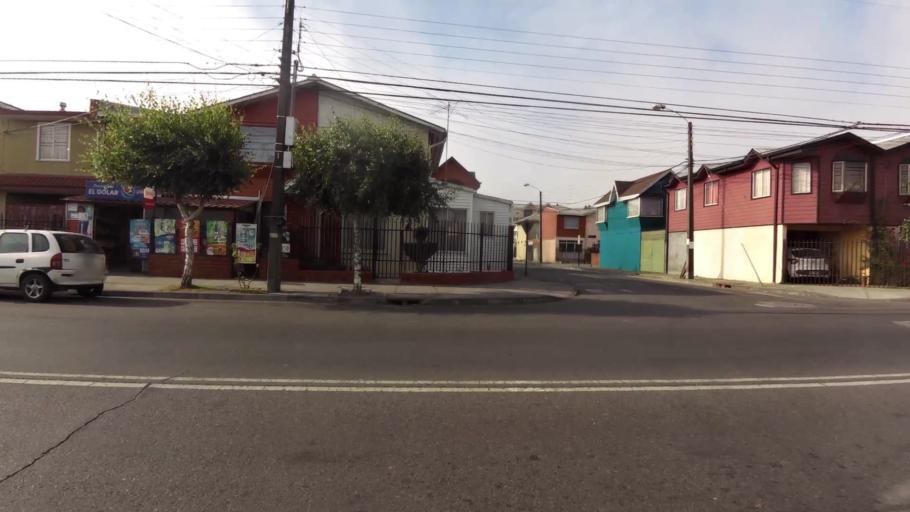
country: CL
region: Biobio
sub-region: Provincia de Concepcion
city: Concepcion
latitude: -36.7978
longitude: -73.1094
